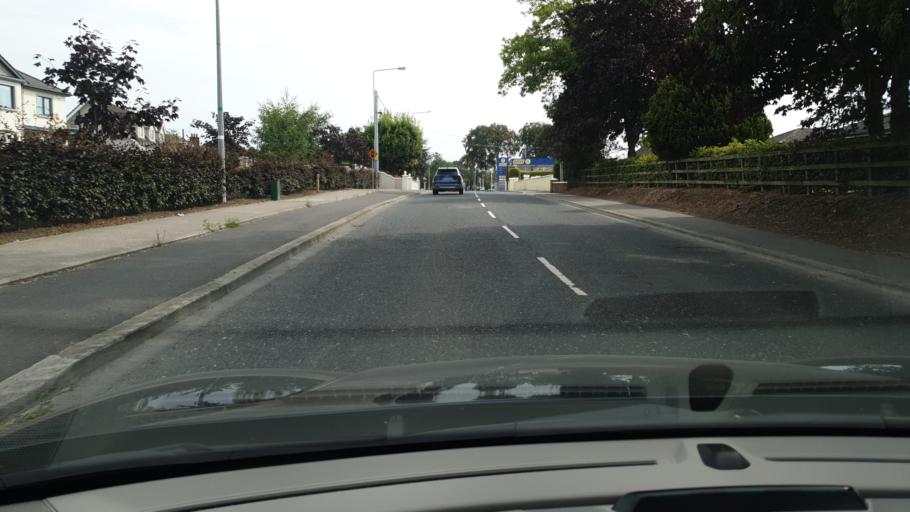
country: IE
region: Leinster
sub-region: An Mhi
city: Navan
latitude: 53.6491
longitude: -6.6562
